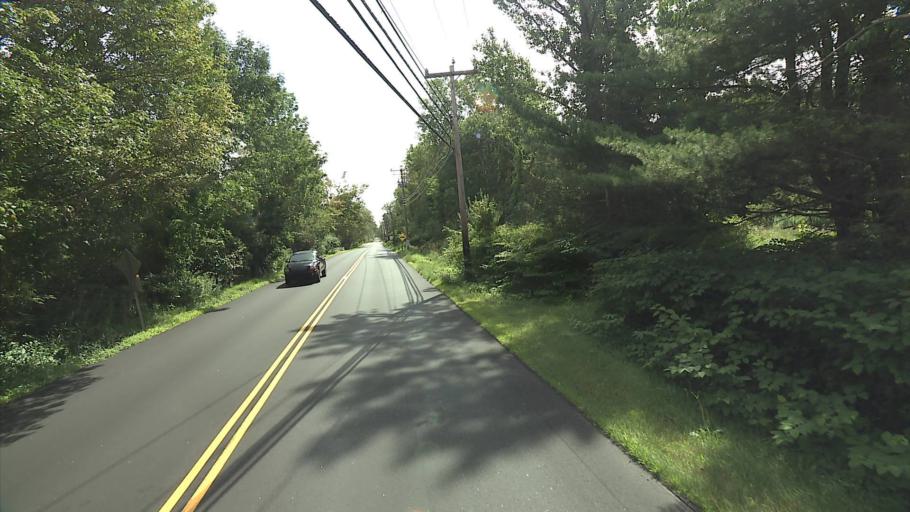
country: US
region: Connecticut
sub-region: Windham County
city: South Woodstock
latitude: 41.9546
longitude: -72.0454
